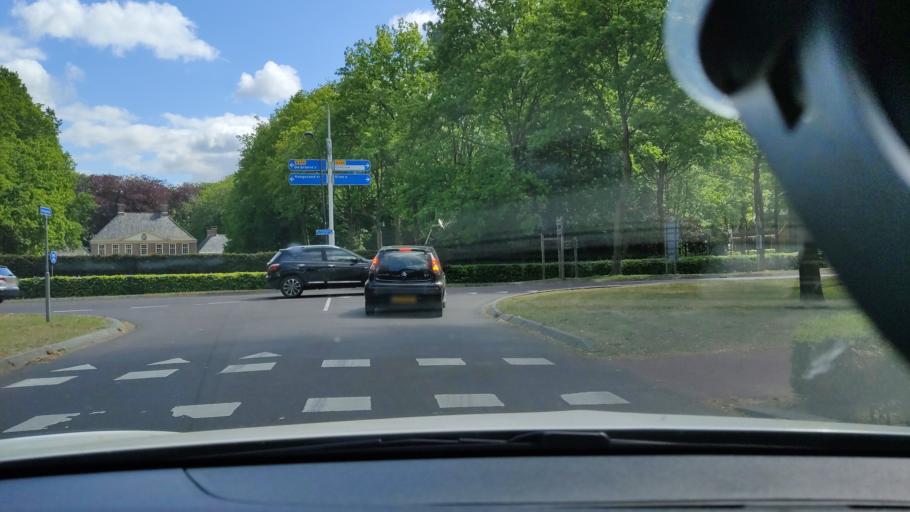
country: NL
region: Drenthe
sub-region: Gemeente Tynaarlo
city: Zuidlaren
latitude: 53.0972
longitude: 6.6888
